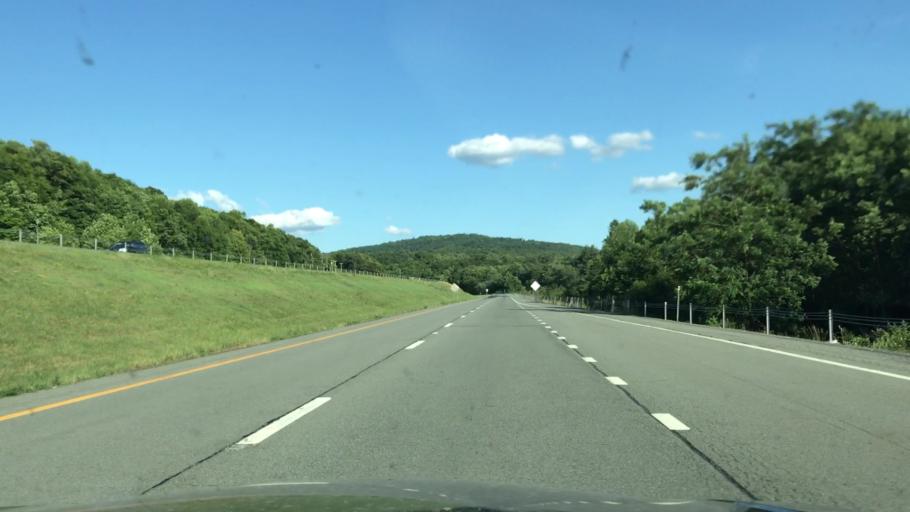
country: US
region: New York
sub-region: Sullivan County
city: Livingston Manor
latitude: 41.9548
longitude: -74.9851
